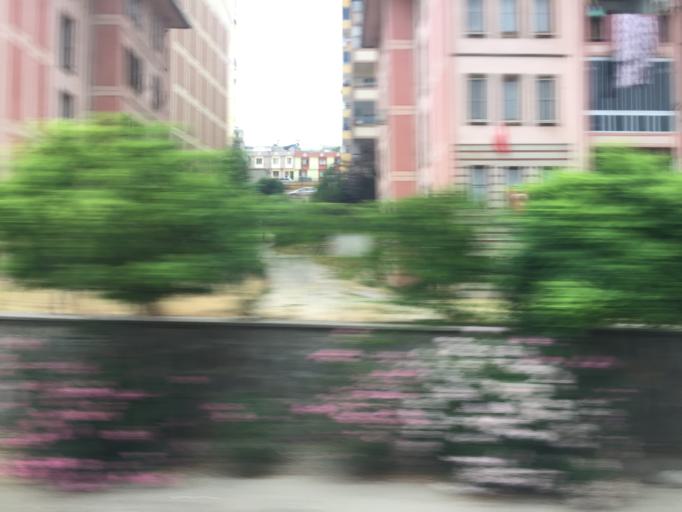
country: TR
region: Gaziantep
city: Gaziantep
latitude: 37.0523
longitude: 37.4206
